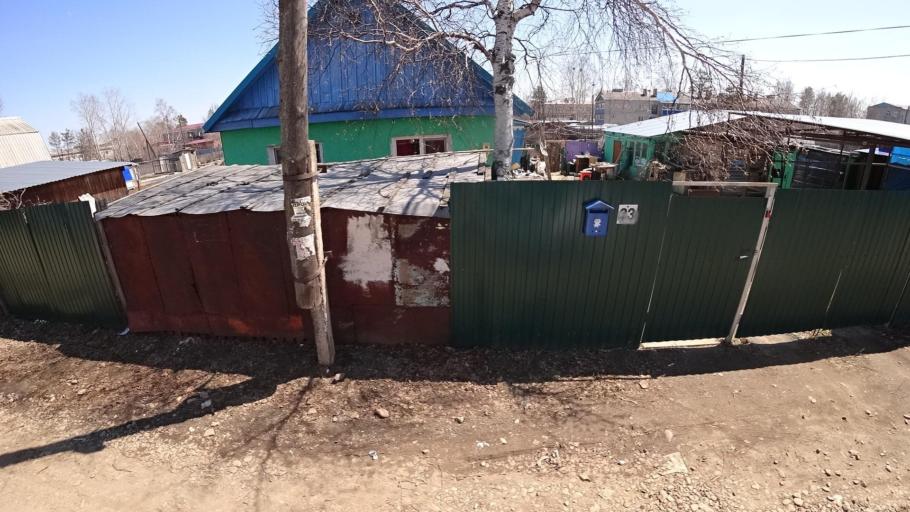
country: RU
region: Khabarovsk Krai
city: Khurba
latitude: 50.4060
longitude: 136.8865
